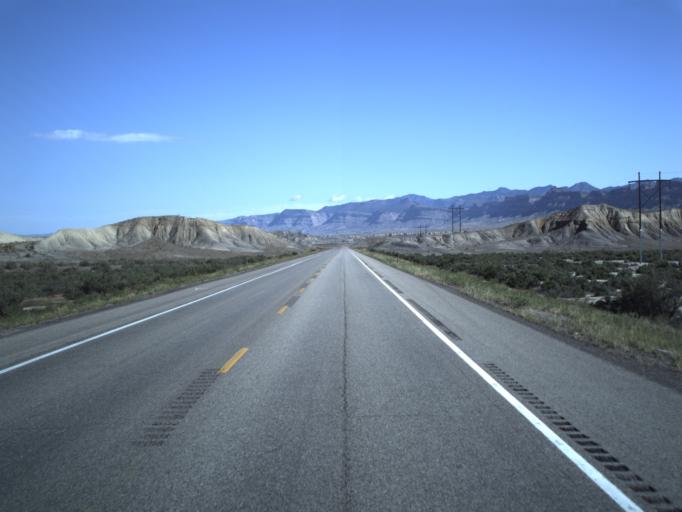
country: US
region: Utah
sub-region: Carbon County
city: East Carbon City
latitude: 39.2443
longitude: -110.3389
